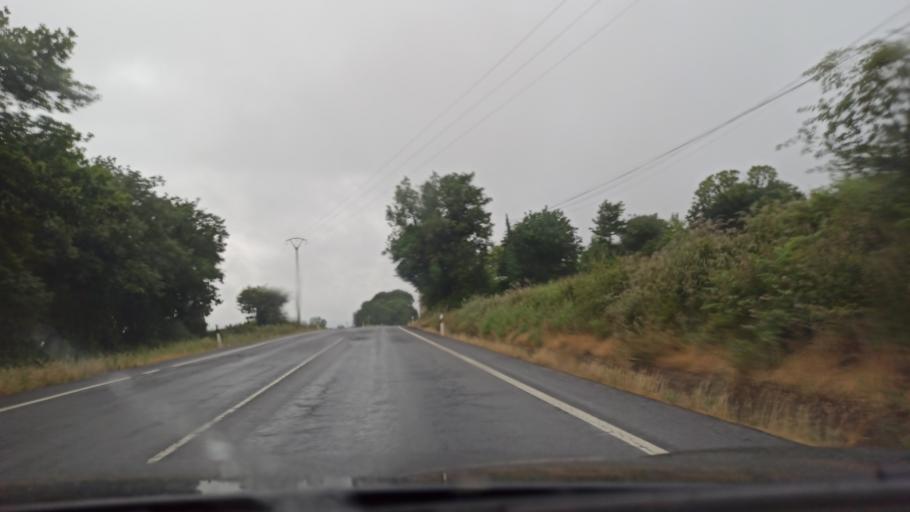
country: ES
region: Galicia
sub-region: Provincia de Lugo
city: Guntin
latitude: 42.9222
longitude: -7.6488
